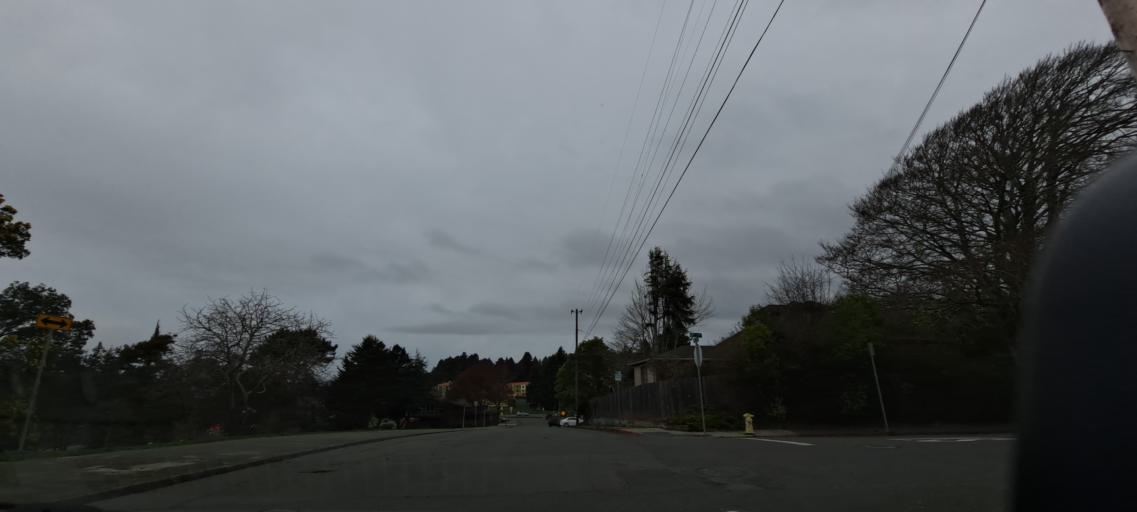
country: US
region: California
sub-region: Humboldt County
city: Arcata
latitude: 40.8704
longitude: -124.0818
